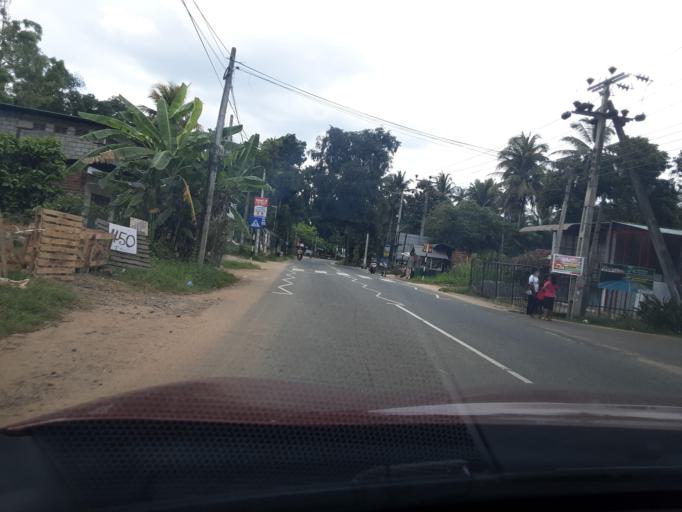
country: LK
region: North Western
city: Kurunegala
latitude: 7.4408
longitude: 80.2062
